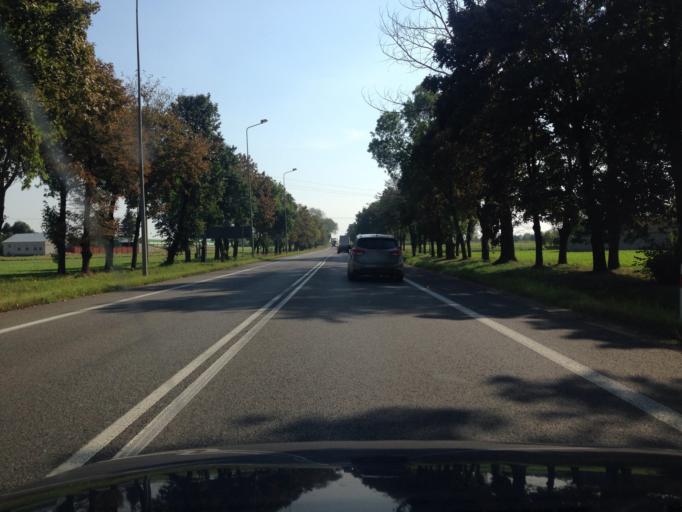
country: PL
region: Masovian Voivodeship
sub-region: Powiat plonski
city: Plonsk
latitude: 52.6043
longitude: 20.3960
